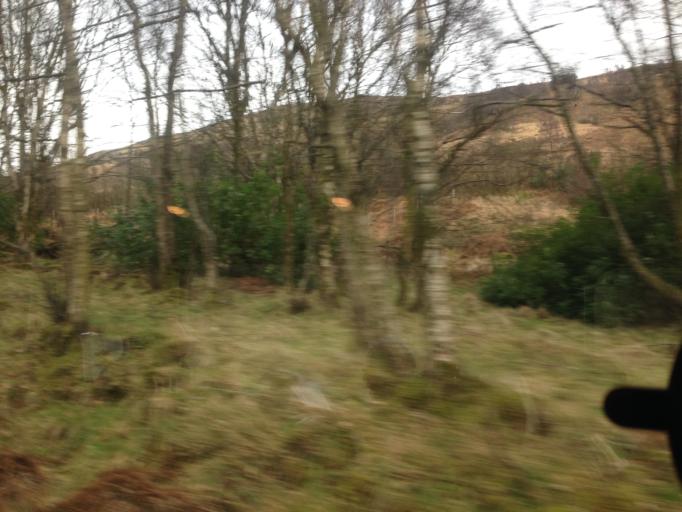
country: GB
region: Scotland
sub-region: Argyll and Bute
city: Garelochhead
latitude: 56.1970
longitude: -4.7344
